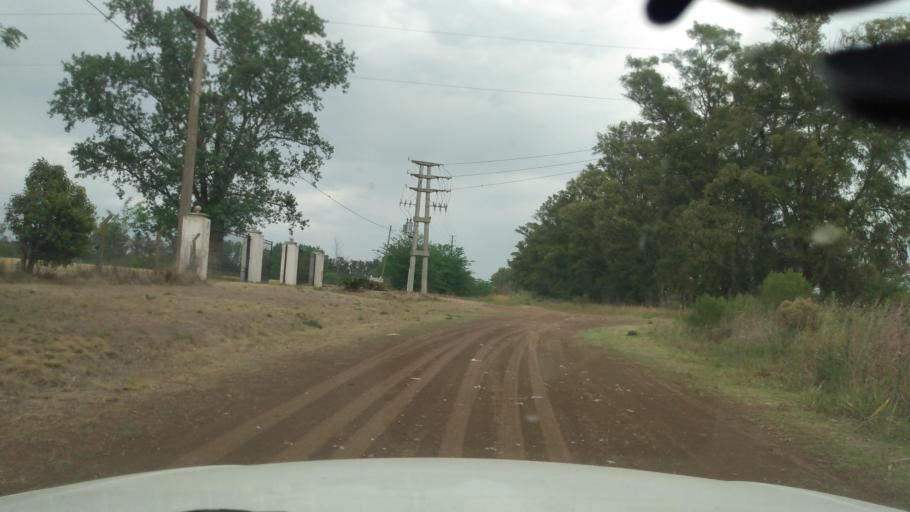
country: AR
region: Buenos Aires
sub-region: Partido de Lujan
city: Lujan
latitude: -34.5508
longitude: -59.1687
